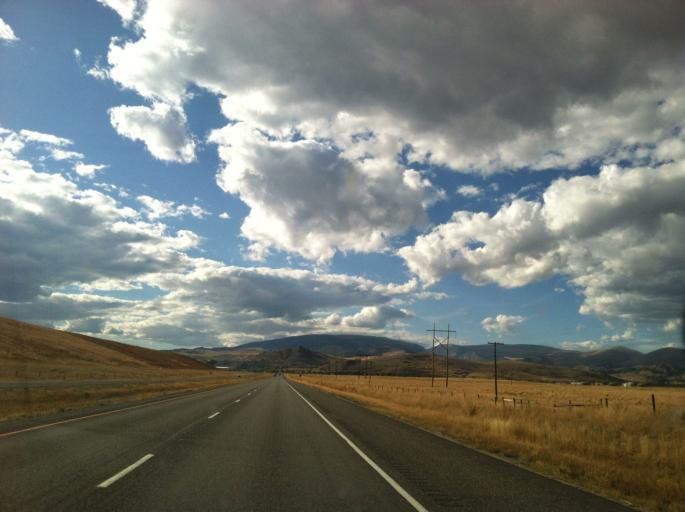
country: US
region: Montana
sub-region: Deer Lodge County
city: Anaconda
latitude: 46.1219
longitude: -112.8821
